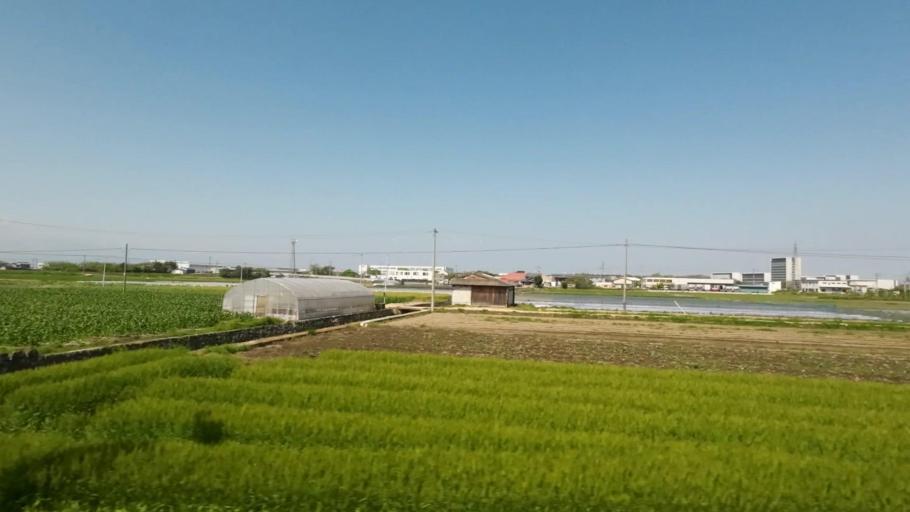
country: JP
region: Kagawa
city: Kan'onjicho
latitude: 34.1125
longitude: 133.6489
